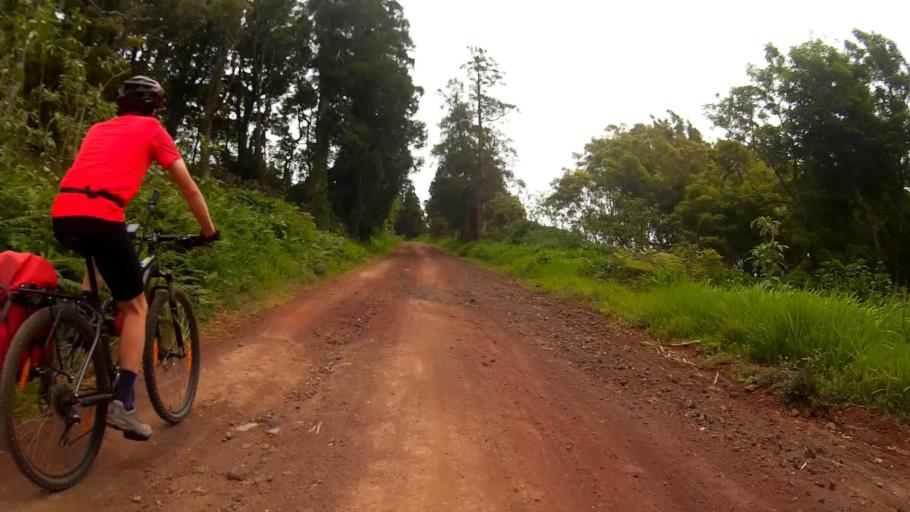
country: PT
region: Azores
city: Ribeira Grande
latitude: 38.5563
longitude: -28.7466
